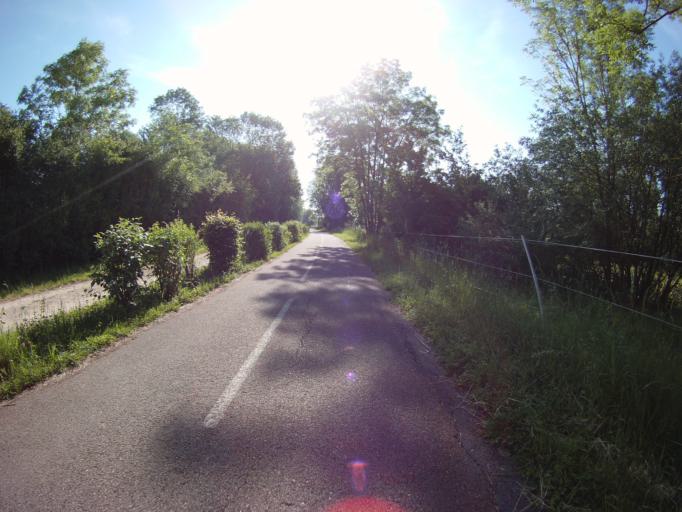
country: FR
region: Lorraine
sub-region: Departement de Meurthe-et-Moselle
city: Eulmont
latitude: 48.7406
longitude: 6.2341
